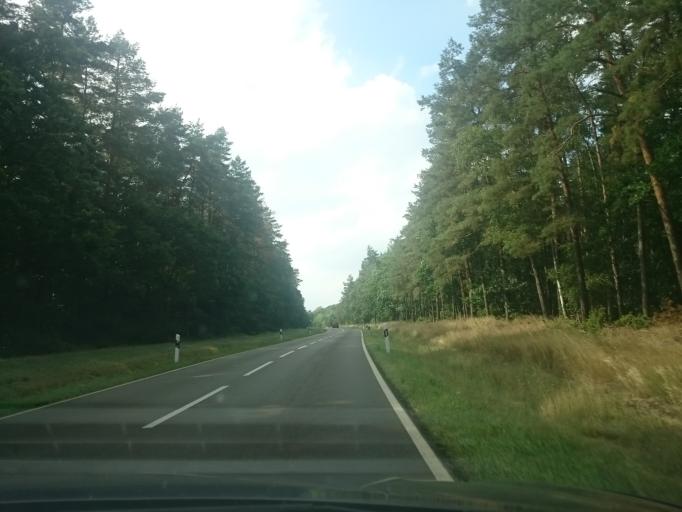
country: DE
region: Mecklenburg-Vorpommern
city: Jatznick
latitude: 53.6392
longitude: 13.9450
